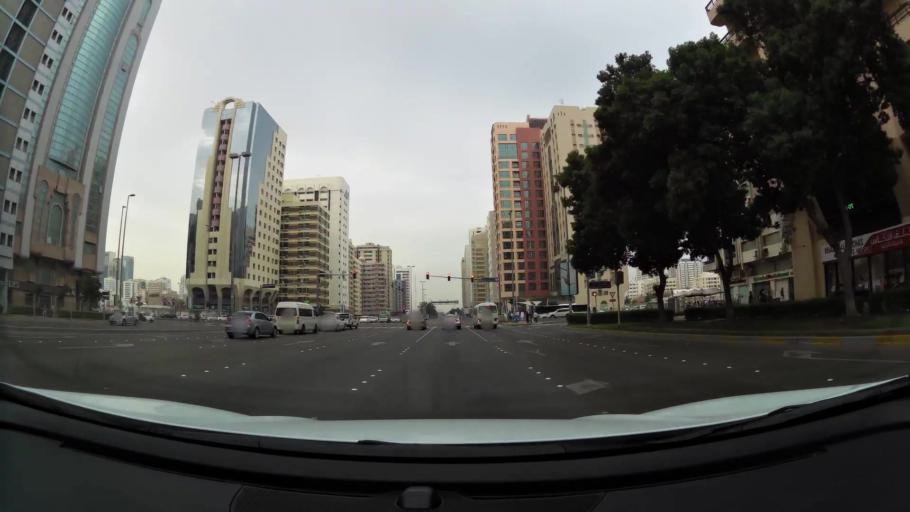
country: AE
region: Abu Dhabi
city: Abu Dhabi
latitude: 24.4796
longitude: 54.3705
